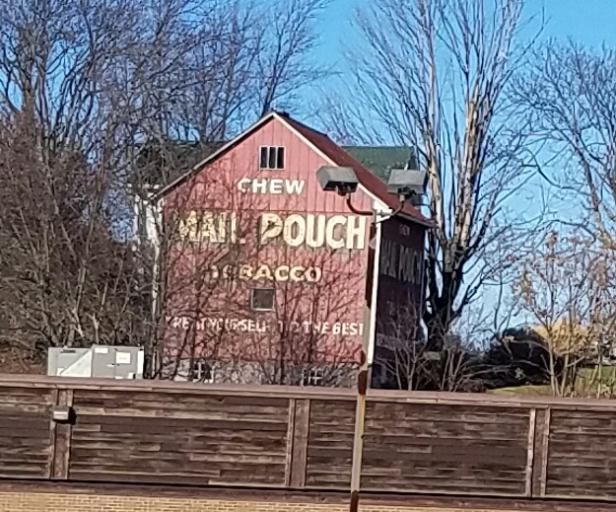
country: US
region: Ohio
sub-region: Belmont County
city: Barnesville
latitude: 39.9886
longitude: -81.1613
